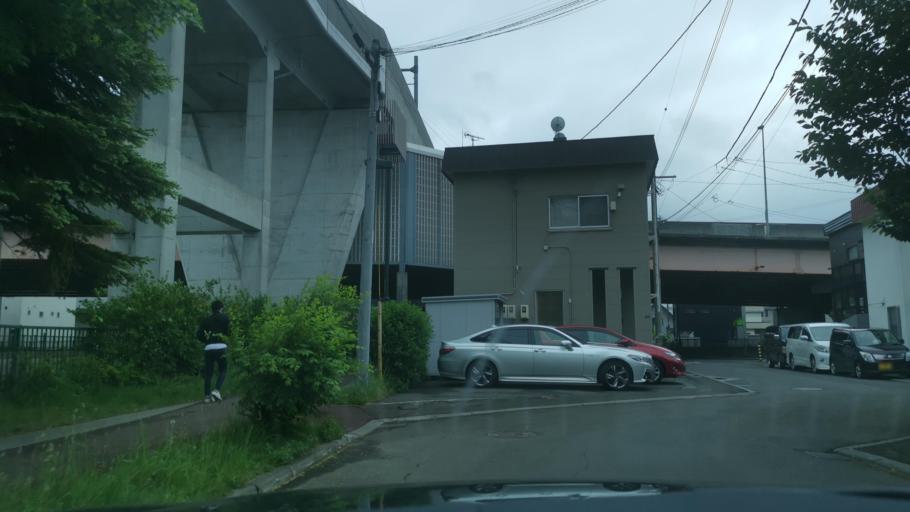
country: JP
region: Hokkaido
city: Sapporo
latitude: 43.1021
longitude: 141.3264
